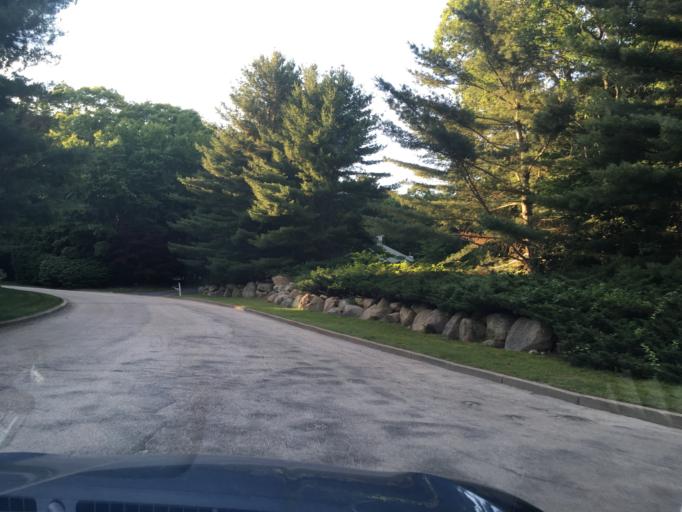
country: US
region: Rhode Island
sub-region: Kent County
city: West Warwick
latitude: 41.6366
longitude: -71.5181
